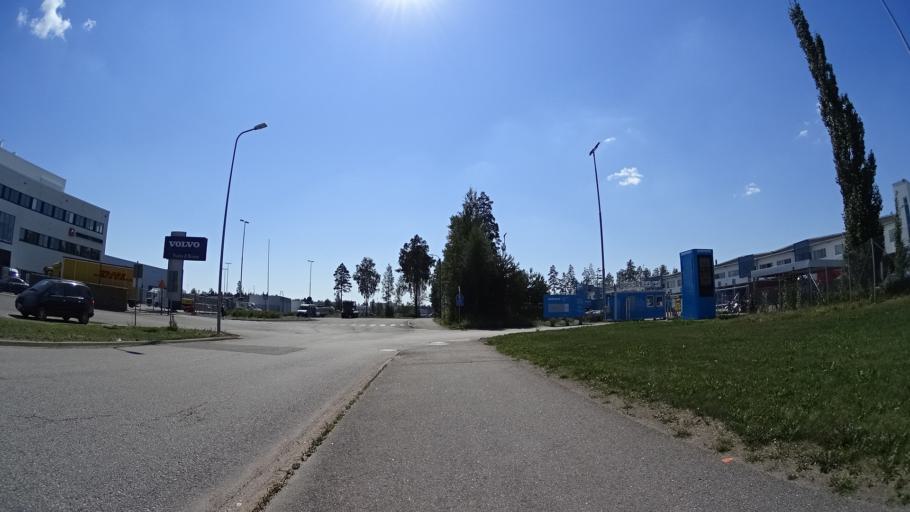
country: FI
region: Uusimaa
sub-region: Helsinki
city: Vantaa
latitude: 60.2991
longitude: 24.9323
